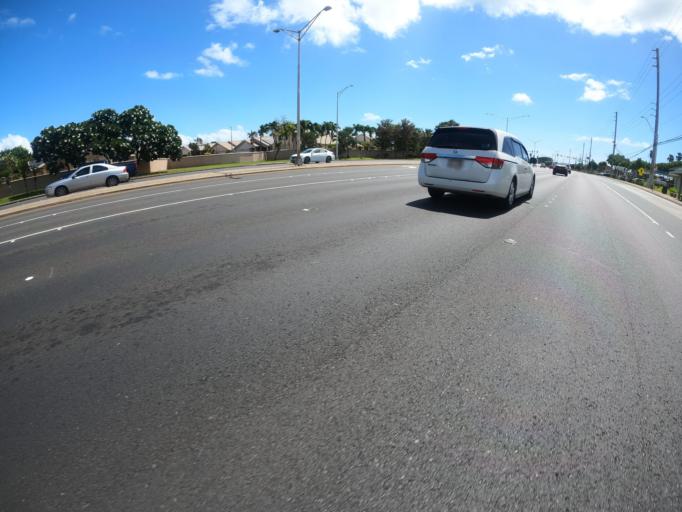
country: US
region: Hawaii
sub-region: Honolulu County
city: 'Ewa Gentry
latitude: 21.3349
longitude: -158.0235
